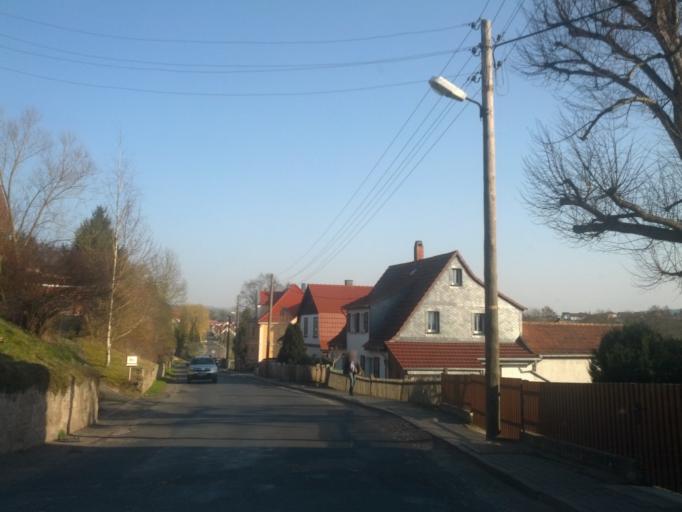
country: DE
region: Thuringia
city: Lauterbach
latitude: 51.0743
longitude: 10.3413
